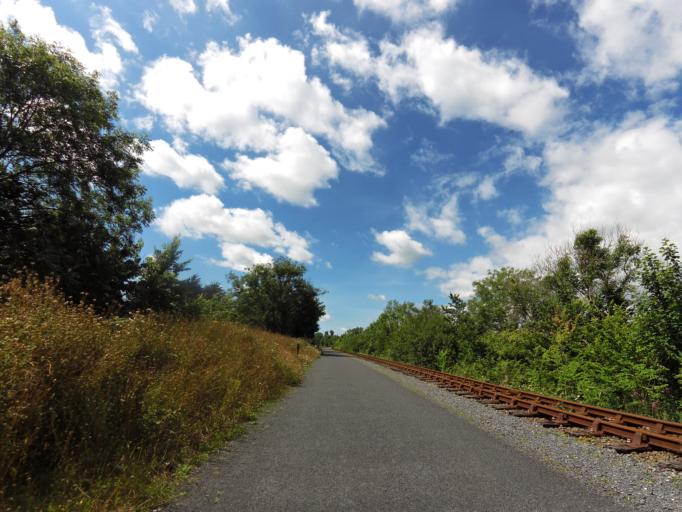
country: IE
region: Leinster
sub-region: Kilkenny
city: Mooncoin
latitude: 52.2472
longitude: -7.2364
